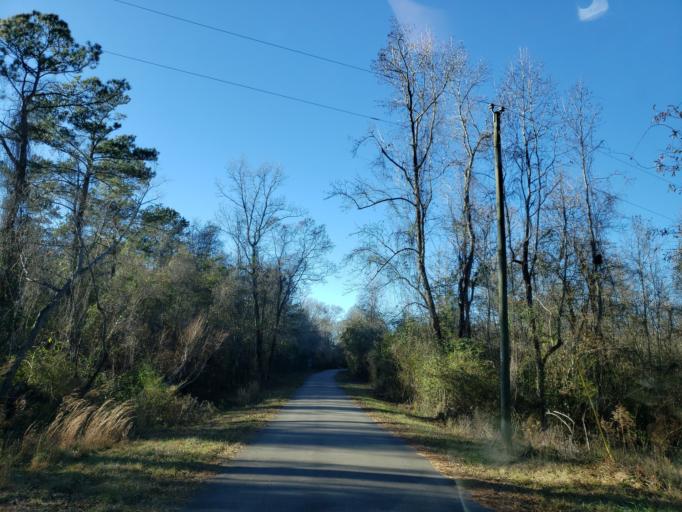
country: US
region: Mississippi
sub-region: Lamar County
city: Arnold Line
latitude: 31.3539
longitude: -89.4542
